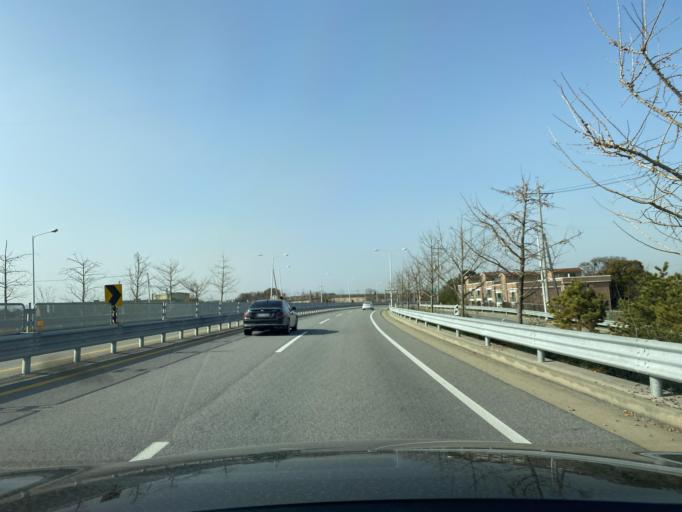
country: KR
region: Chungcheongnam-do
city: Yesan
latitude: 36.7580
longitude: 126.8194
